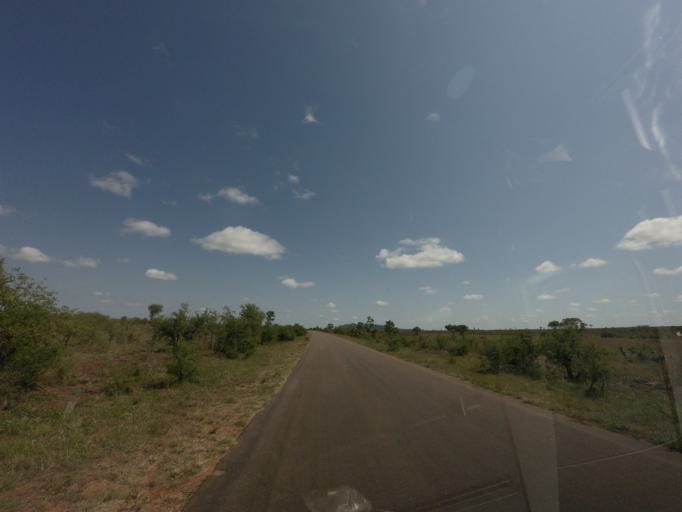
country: ZA
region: Mpumalanga
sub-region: Ehlanzeni District
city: Komatipoort
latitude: -25.0798
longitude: 31.9189
